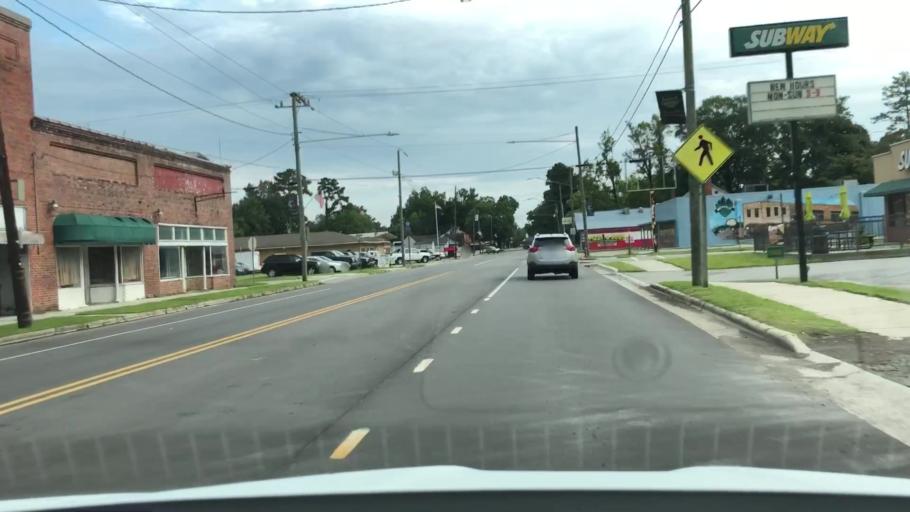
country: US
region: North Carolina
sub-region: Jones County
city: Maysville
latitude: 34.9048
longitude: -77.2315
